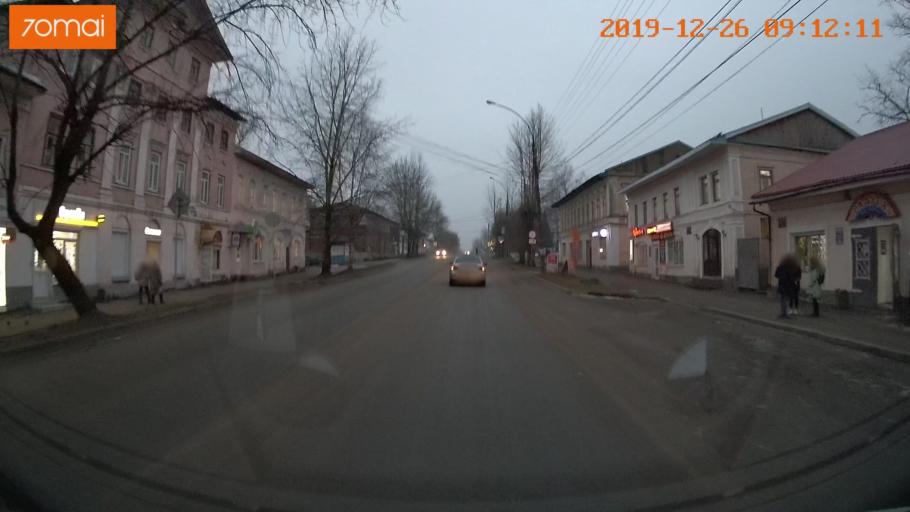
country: RU
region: Vologda
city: Gryazovets
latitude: 58.8797
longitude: 40.2532
